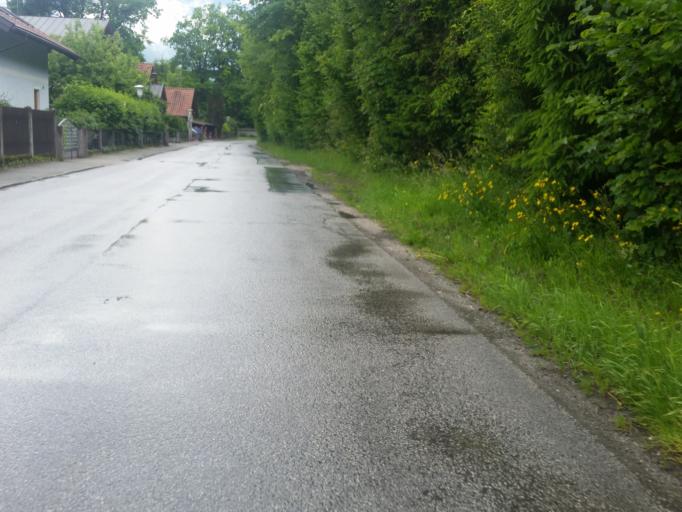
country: AT
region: Salzburg
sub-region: Salzburg Stadt
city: Salzburg
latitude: 47.7813
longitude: 13.0023
